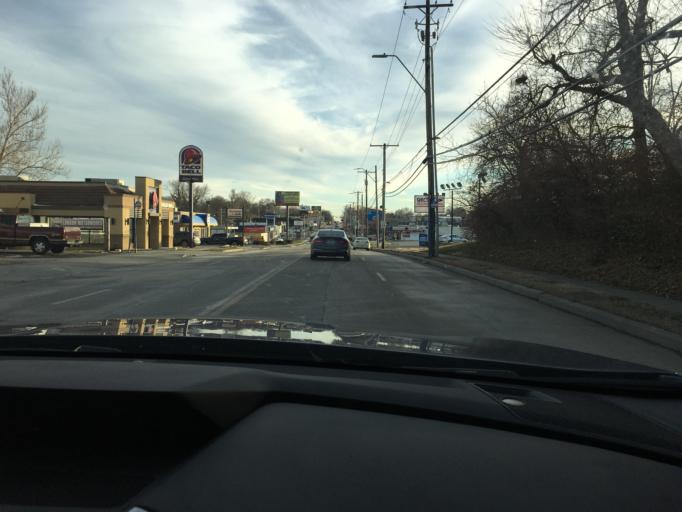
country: US
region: Kansas
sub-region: Johnson County
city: Leawood
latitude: 38.9795
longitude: -94.5948
